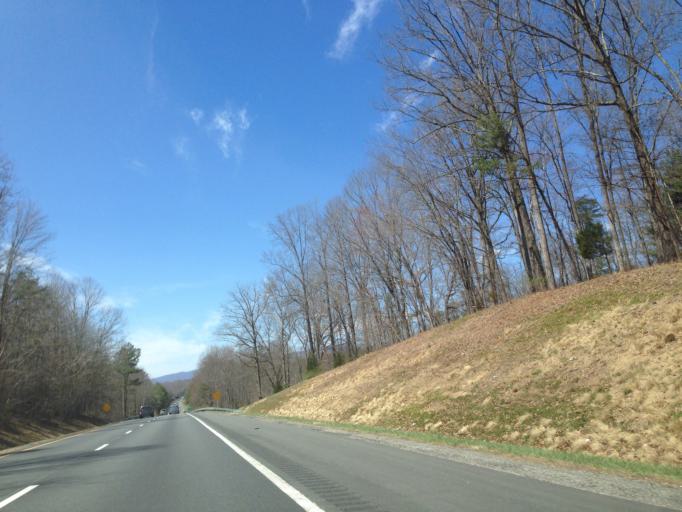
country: US
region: Virginia
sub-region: Albemarle County
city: Crozet
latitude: 38.0310
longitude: -78.6665
